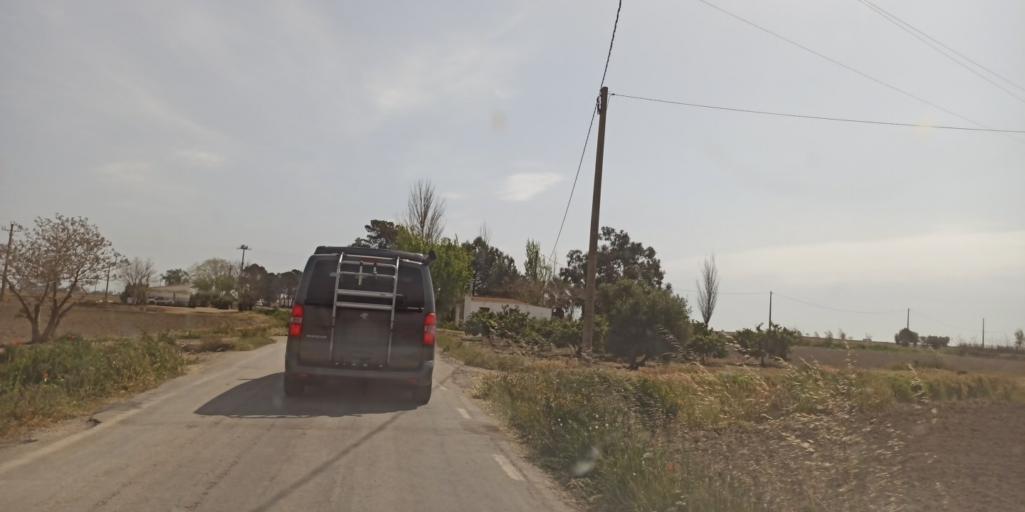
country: ES
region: Catalonia
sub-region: Provincia de Tarragona
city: Deltebre
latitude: 40.6468
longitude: 0.7090
